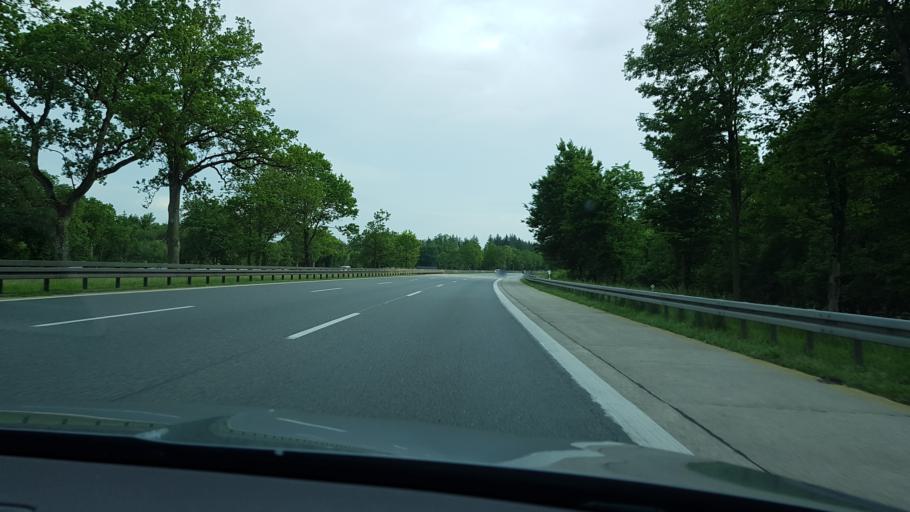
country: DE
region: Bavaria
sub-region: Upper Bavaria
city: Neuried
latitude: 48.0627
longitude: 11.4744
